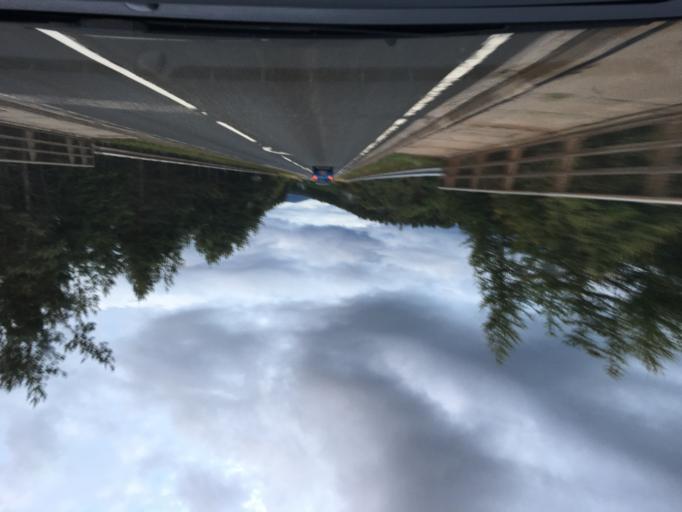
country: GB
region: Scotland
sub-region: Highland
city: Aviemore
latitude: 57.2799
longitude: -3.8311
